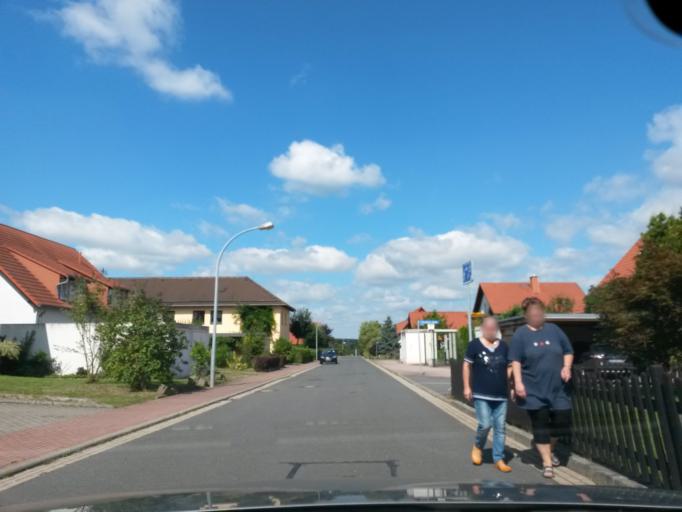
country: DE
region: Thuringia
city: Hermsdorf
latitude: 50.8933
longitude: 11.8686
